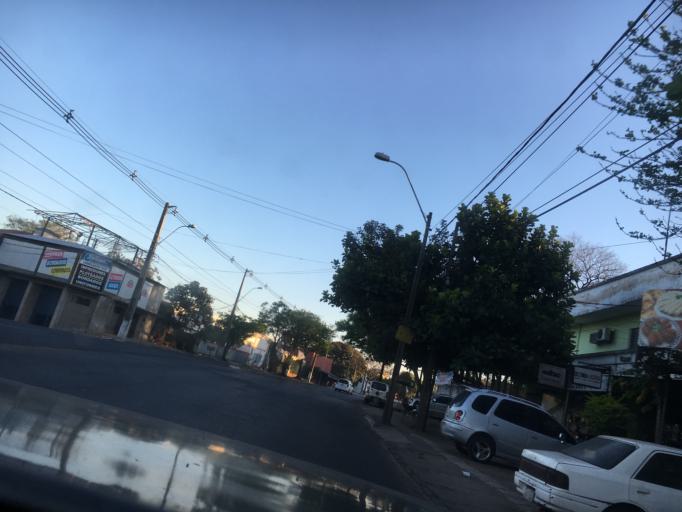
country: PY
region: Asuncion
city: Asuncion
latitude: -25.3023
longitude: -57.6323
